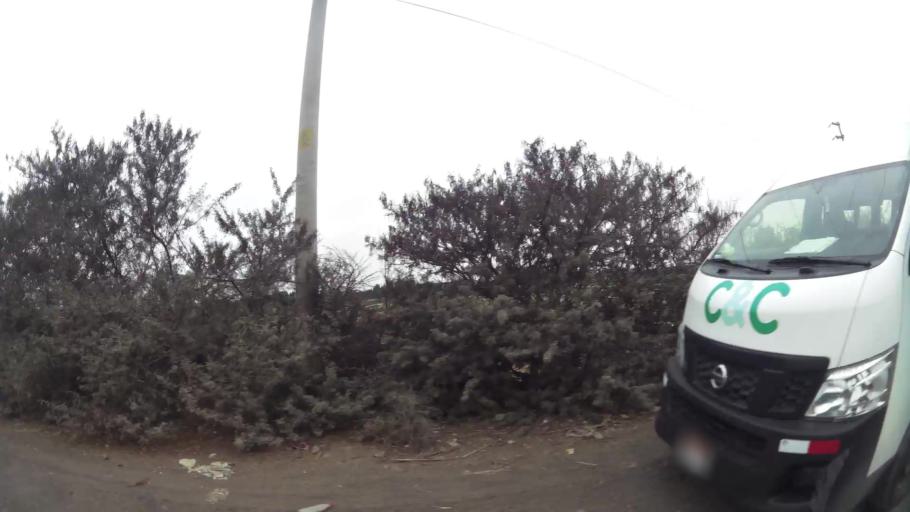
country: PE
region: Ica
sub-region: Provincia de Pisco
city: Pisco
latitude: -13.7456
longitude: -76.1930
